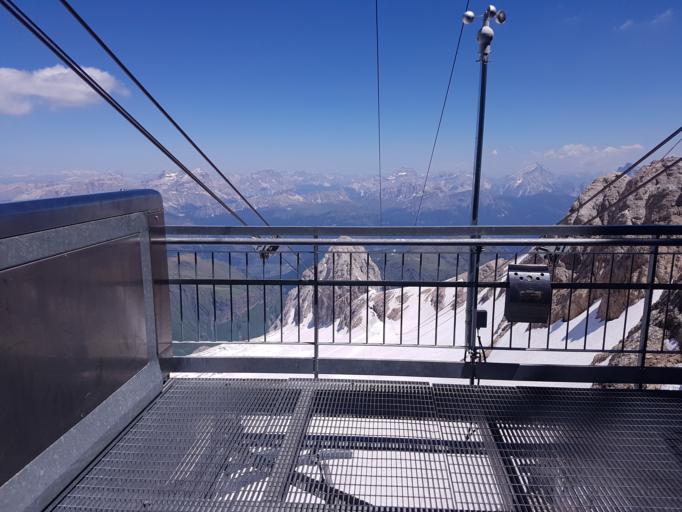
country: IT
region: Veneto
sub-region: Provincia di Belluno
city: Pie' Falcade
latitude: 46.4335
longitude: 11.8624
